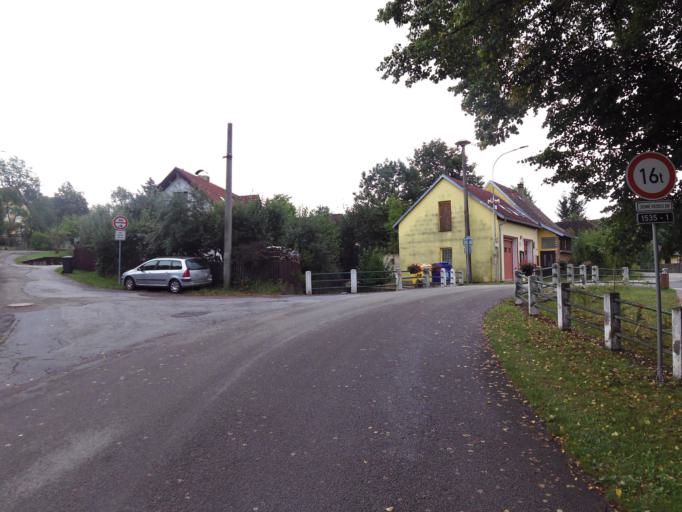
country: CZ
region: Jihocesky
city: Chlum u Trebone
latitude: 48.9794
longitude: 14.9525
